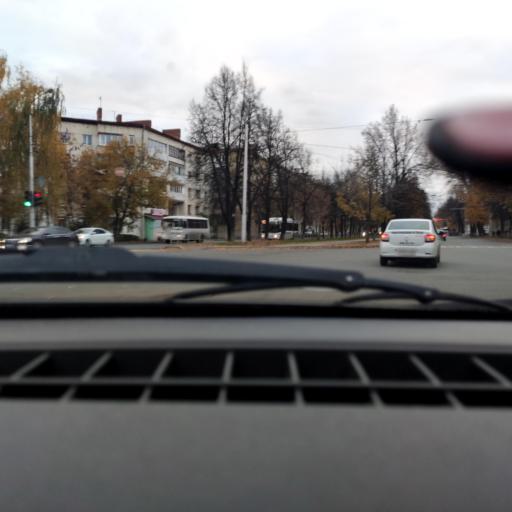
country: RU
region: Bashkortostan
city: Ufa
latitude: 54.8148
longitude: 56.1044
